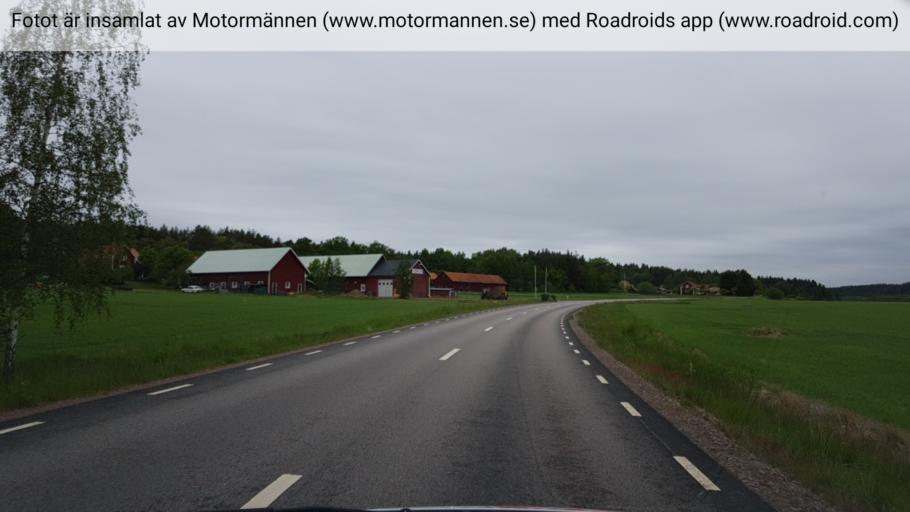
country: SE
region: Kalmar
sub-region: Vasterviks Kommun
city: Forserum
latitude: 57.9400
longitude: 16.4554
